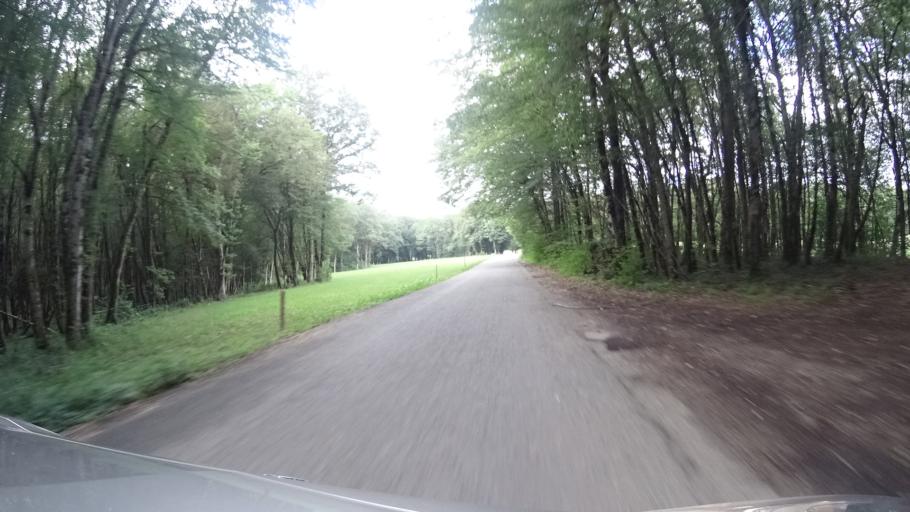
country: FR
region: Franche-Comte
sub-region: Departement du Doubs
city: Nancray
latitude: 47.2292
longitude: 6.1620
